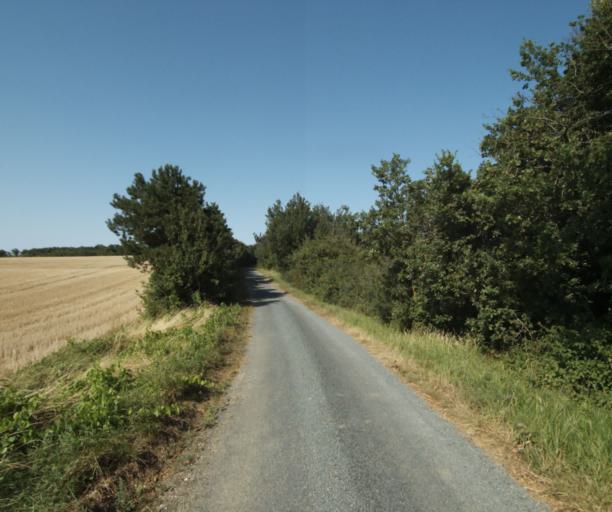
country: FR
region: Midi-Pyrenees
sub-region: Departement de la Haute-Garonne
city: Saint-Felix-Lauragais
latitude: 43.4183
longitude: 1.8426
